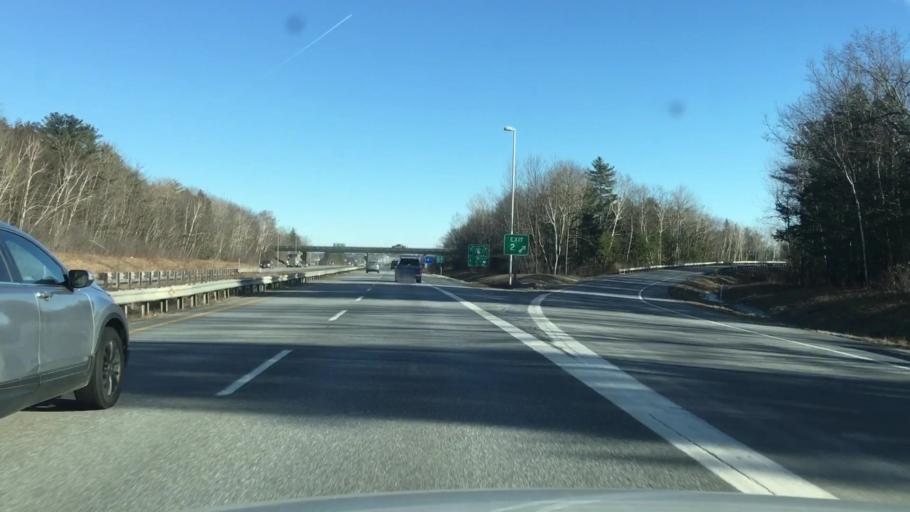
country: US
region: Maine
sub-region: Penobscot County
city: Bangor
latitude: 44.7862
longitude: -68.7980
